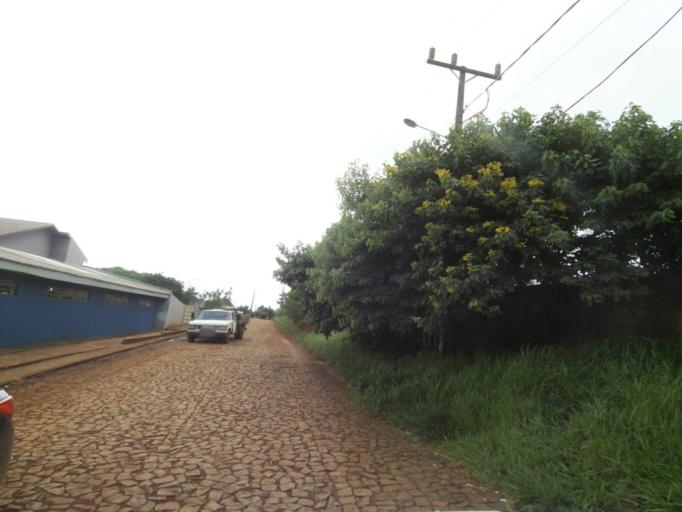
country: BR
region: Parana
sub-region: Pitanga
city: Pitanga
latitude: -24.9408
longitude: -51.8708
